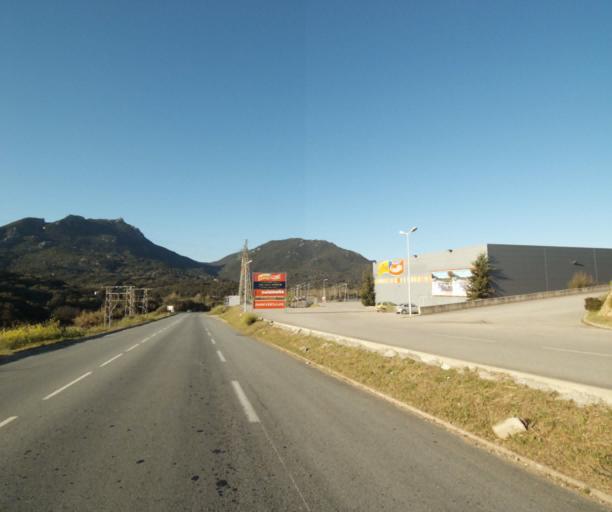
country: FR
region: Corsica
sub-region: Departement de la Corse-du-Sud
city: Propriano
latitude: 41.6632
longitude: 8.9184
